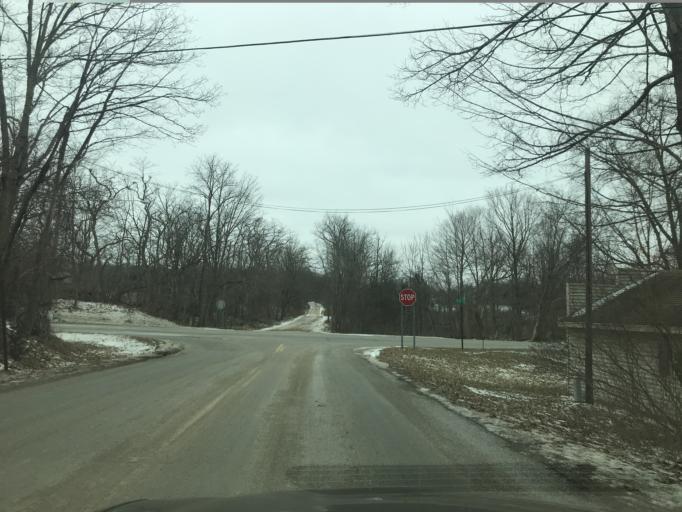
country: US
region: Michigan
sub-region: Lenawee County
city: Manitou Beach-Devils Lake
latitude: 42.0493
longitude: -84.3257
